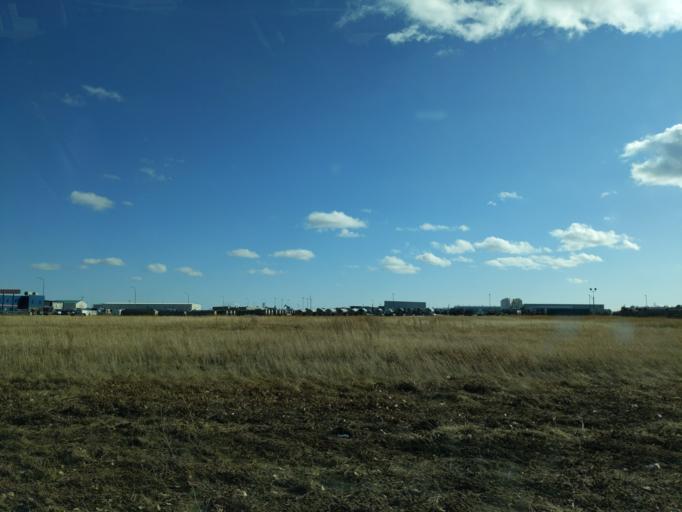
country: CA
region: Saskatchewan
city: Lloydminster
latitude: 53.2998
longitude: -110.0384
